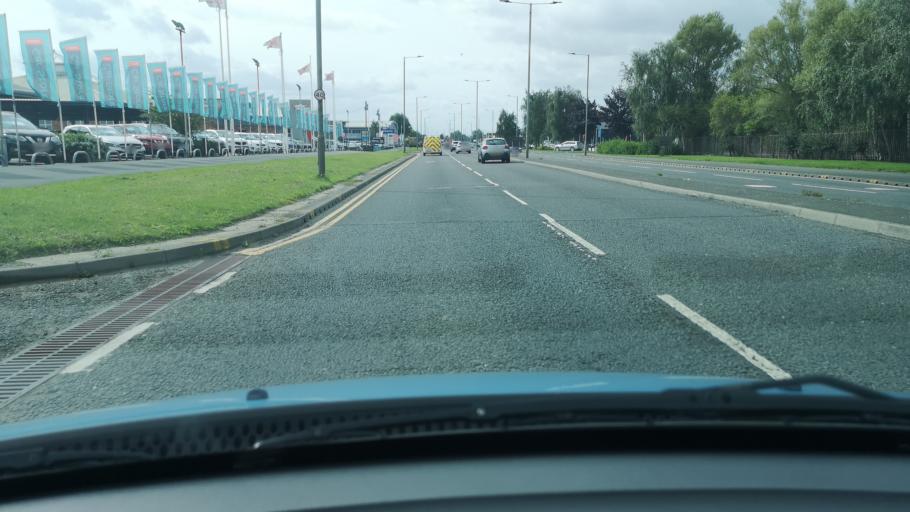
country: GB
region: England
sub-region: Doncaster
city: Kirk Sandall
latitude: 53.5463
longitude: -1.0946
